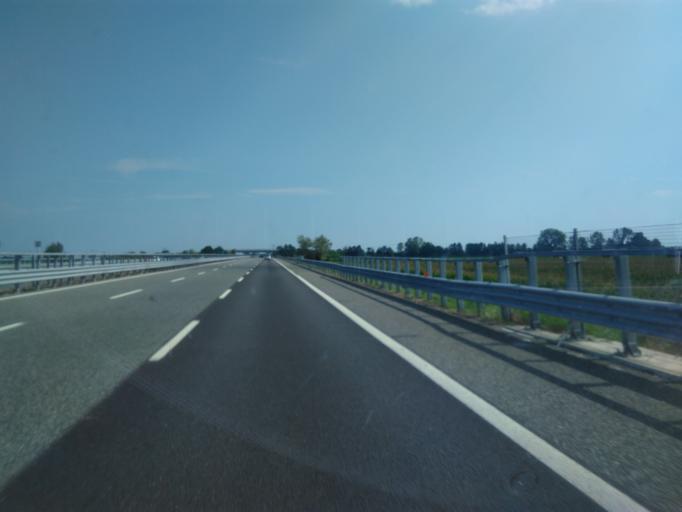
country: IT
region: Piedmont
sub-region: Provincia di Alessandria
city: Villanova Monferrato
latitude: 45.1970
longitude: 8.4914
